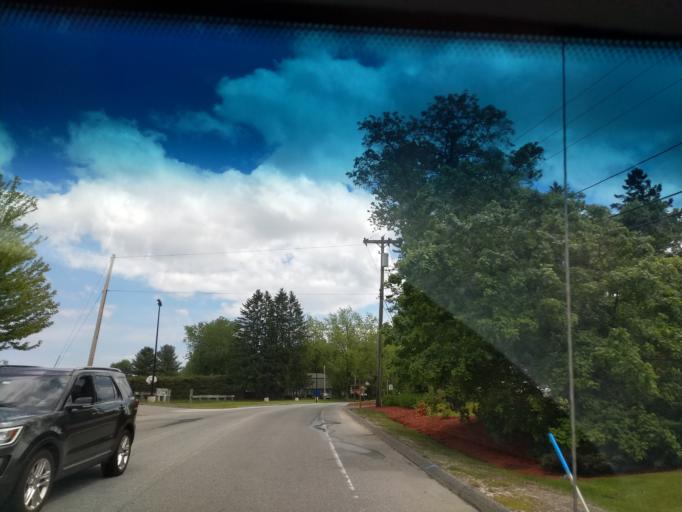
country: US
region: Maine
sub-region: Cumberland County
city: Falmouth
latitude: 43.7463
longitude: -70.2944
